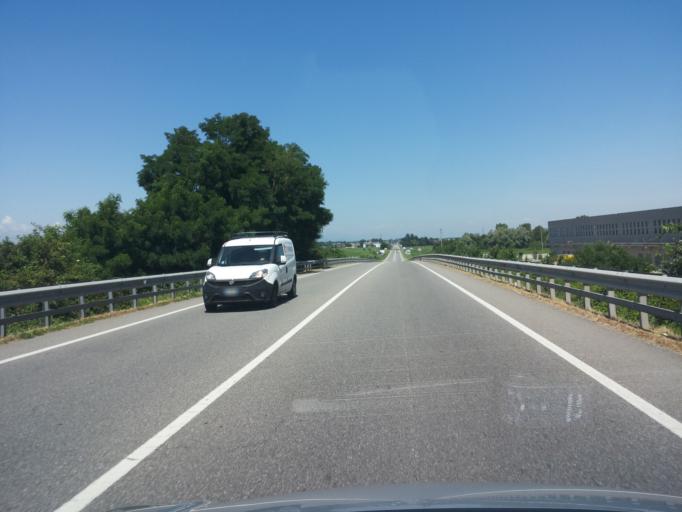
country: IT
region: Piedmont
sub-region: Provincia di Vercelli
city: Caresanablot
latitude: 45.3290
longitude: 8.3897
